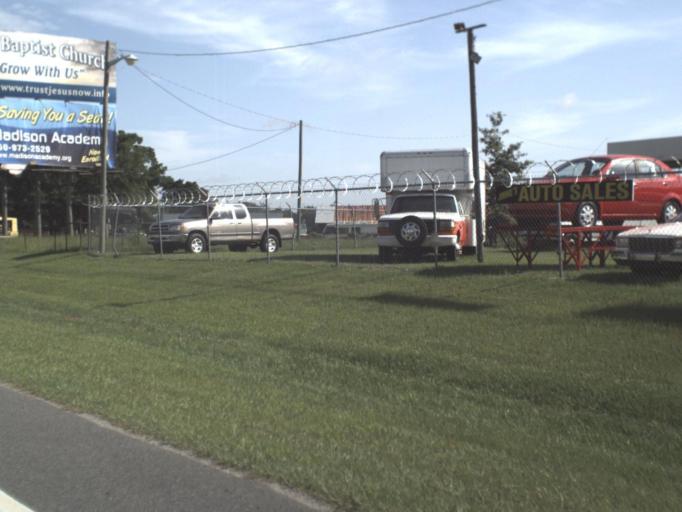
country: US
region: Florida
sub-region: Madison County
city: Madison
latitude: 30.4036
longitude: -83.3627
